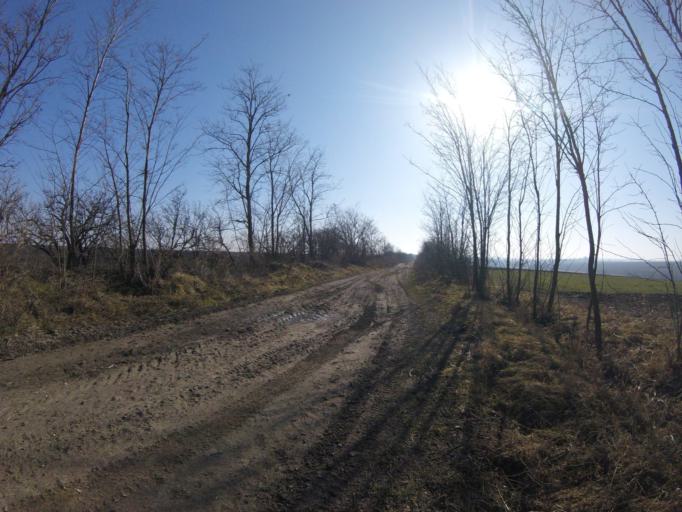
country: HU
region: Komarom-Esztergom
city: Csaszar
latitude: 47.5339
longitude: 18.1942
